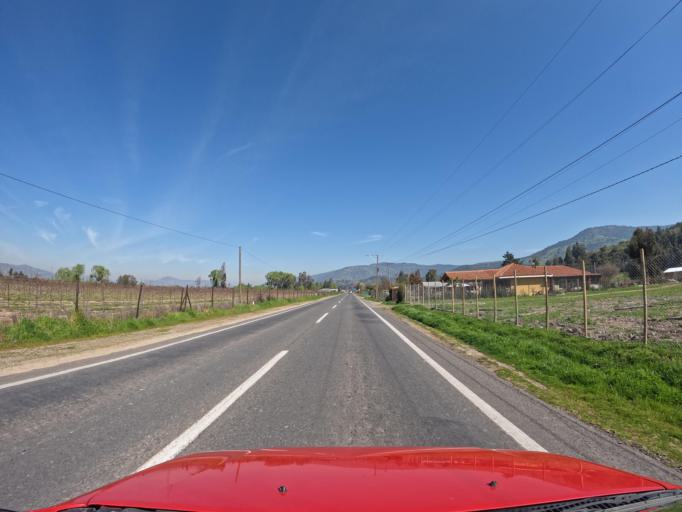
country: CL
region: Maule
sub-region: Provincia de Curico
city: Rauco
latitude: -34.9785
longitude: -71.3961
